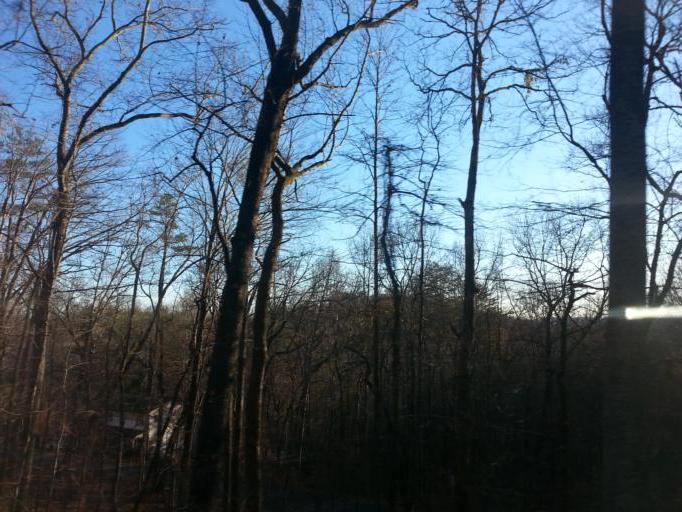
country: US
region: Tennessee
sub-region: Anderson County
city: Rocky Top
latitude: 36.2329
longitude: -84.1177
